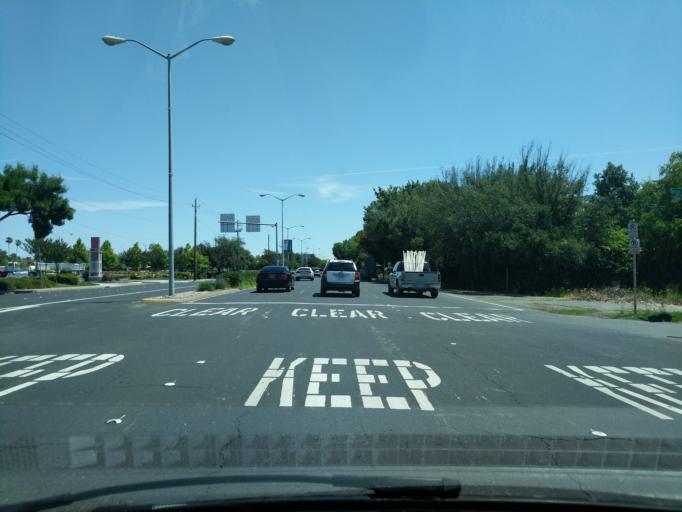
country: US
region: California
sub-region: Contra Costa County
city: Pleasant Hill
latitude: 37.9630
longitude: -122.0607
